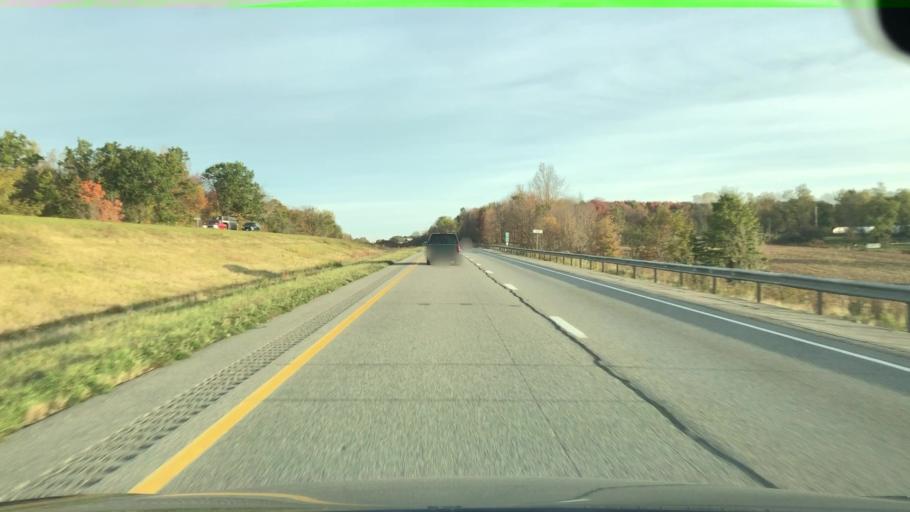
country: US
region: Pennsylvania
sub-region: Mercer County
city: Stoneboro
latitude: 41.3027
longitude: -80.1578
